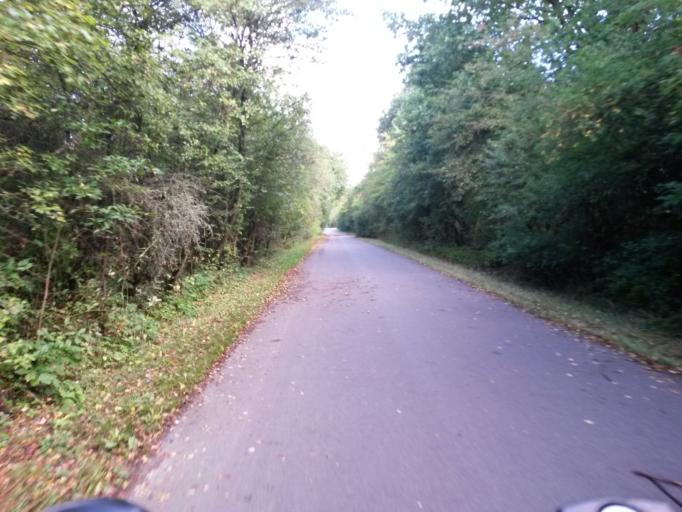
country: DE
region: Brandenburg
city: Templin
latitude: 53.1952
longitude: 13.5148
